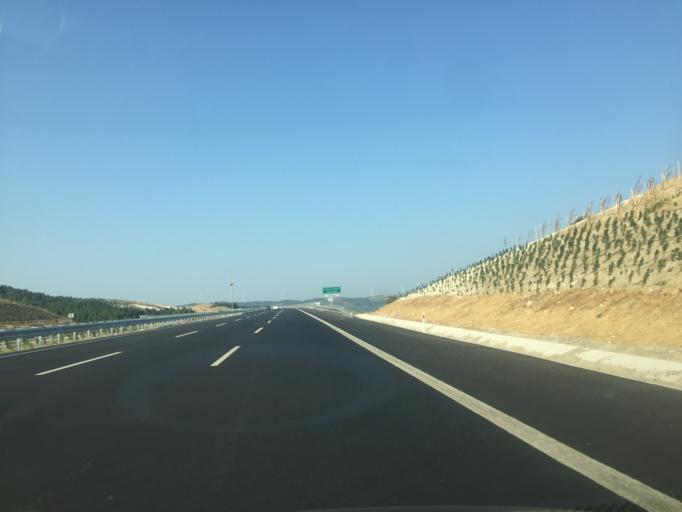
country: TR
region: Manisa
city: Zeytinliova
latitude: 39.0082
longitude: 27.7448
